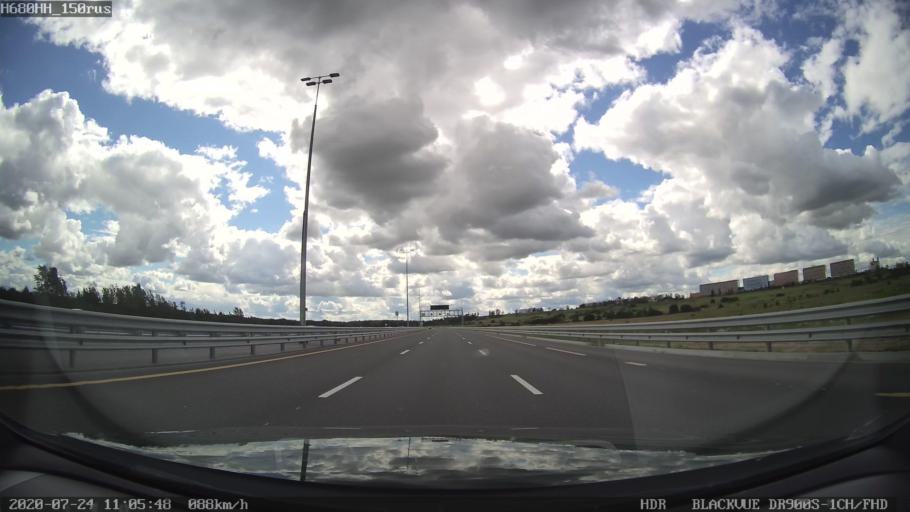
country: RU
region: St.-Petersburg
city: Shushary
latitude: 59.7721
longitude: 30.3624
